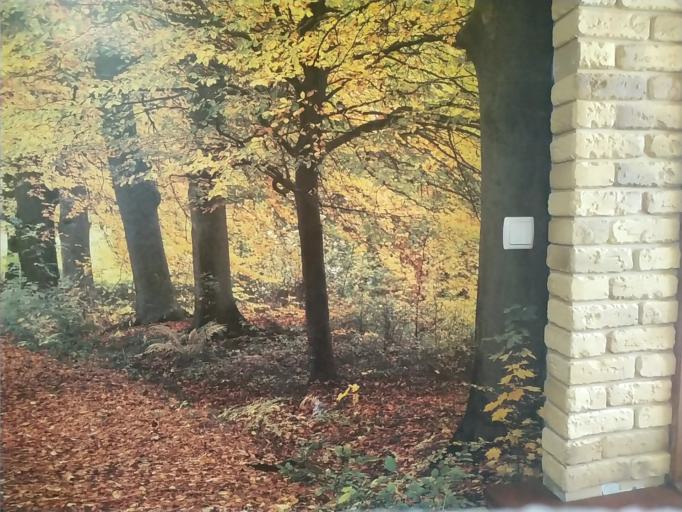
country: RU
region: Tverskaya
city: Vyshniy Volochek
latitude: 57.6173
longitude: 34.5892
